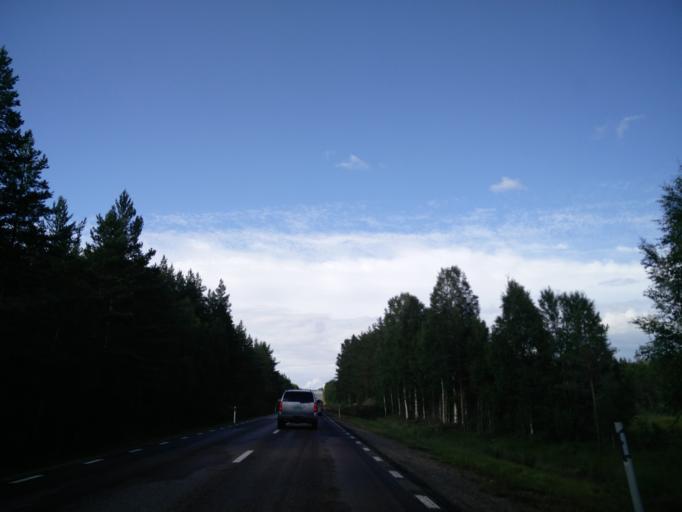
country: SE
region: Vaermland
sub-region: Hagfors Kommun
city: Ekshaerad
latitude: 60.4627
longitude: 13.2984
